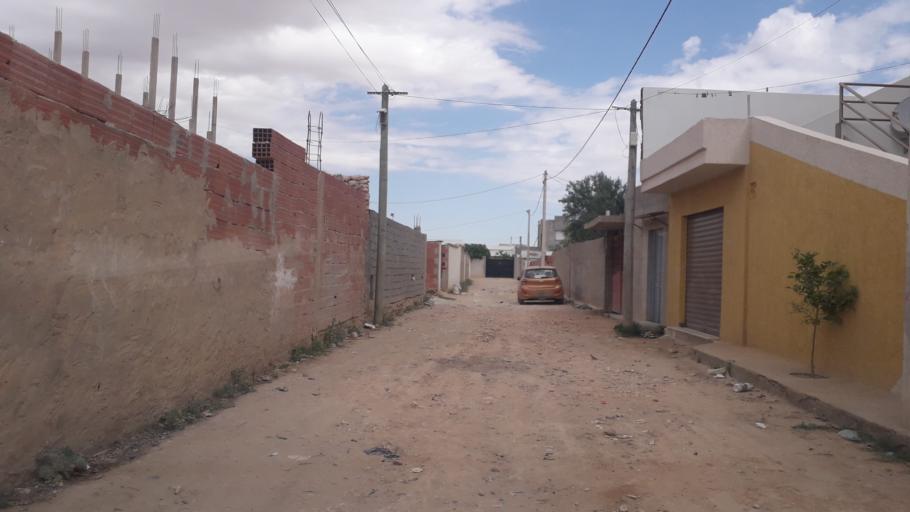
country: TN
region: Safaqis
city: Al Qarmadah
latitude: 34.8409
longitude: 10.7740
